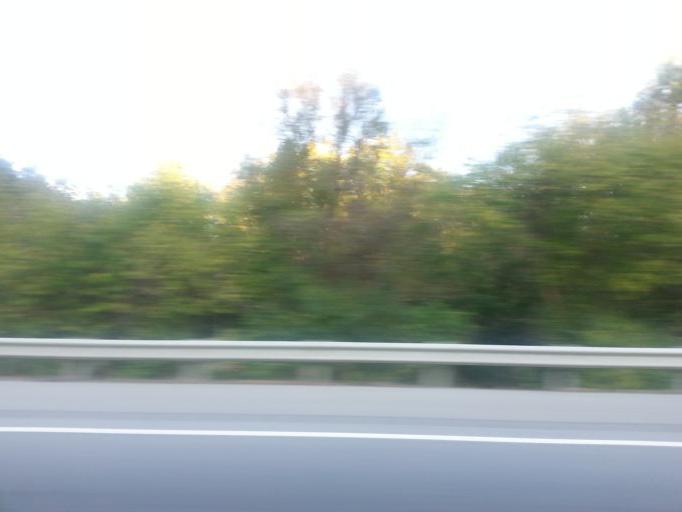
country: US
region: Tennessee
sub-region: Anderson County
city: Norris
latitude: 36.1315
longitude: -84.0367
